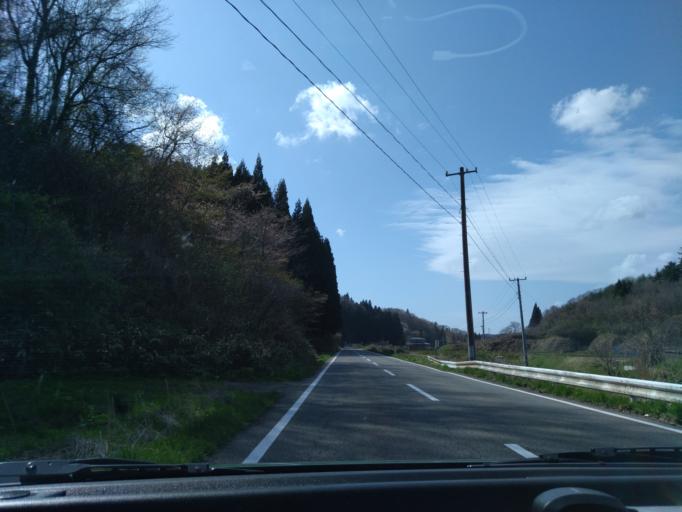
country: JP
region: Akita
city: Akita
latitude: 39.7060
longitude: 140.2105
